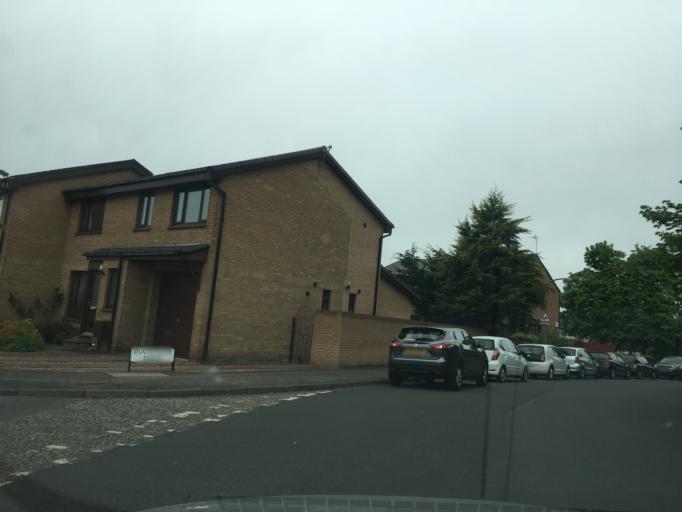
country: GB
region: Scotland
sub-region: Midlothian
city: Loanhead
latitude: 55.9036
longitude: -3.1976
